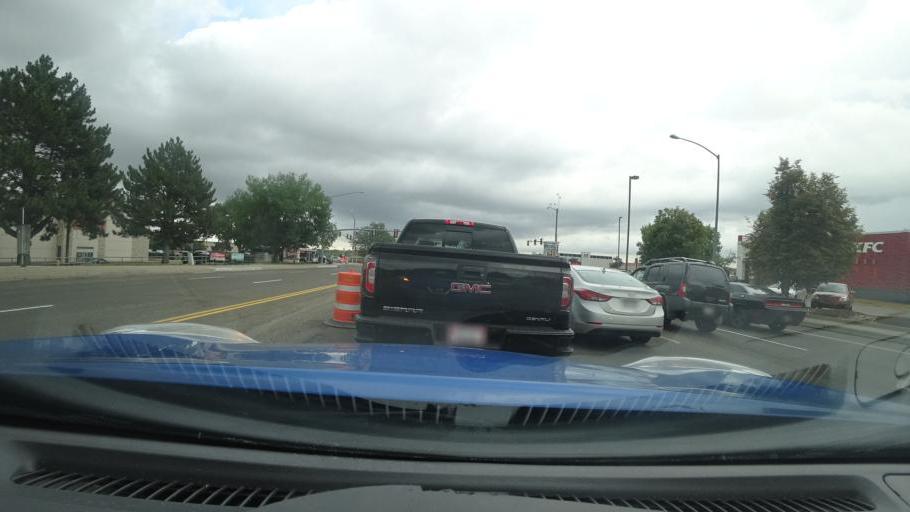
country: US
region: Colorado
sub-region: Adams County
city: Aurora
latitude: 39.6966
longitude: -104.8108
